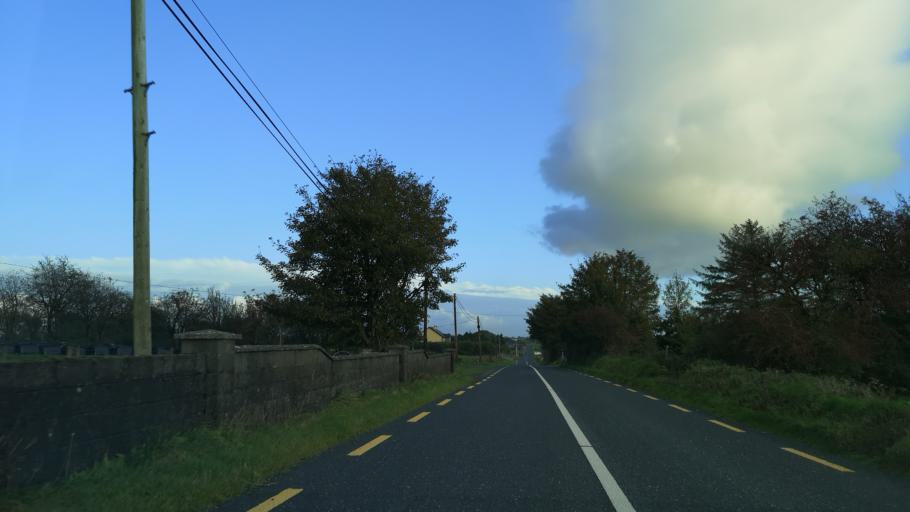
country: IE
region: Connaught
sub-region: Roscommon
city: Castlerea
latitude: 53.6209
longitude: -8.6119
